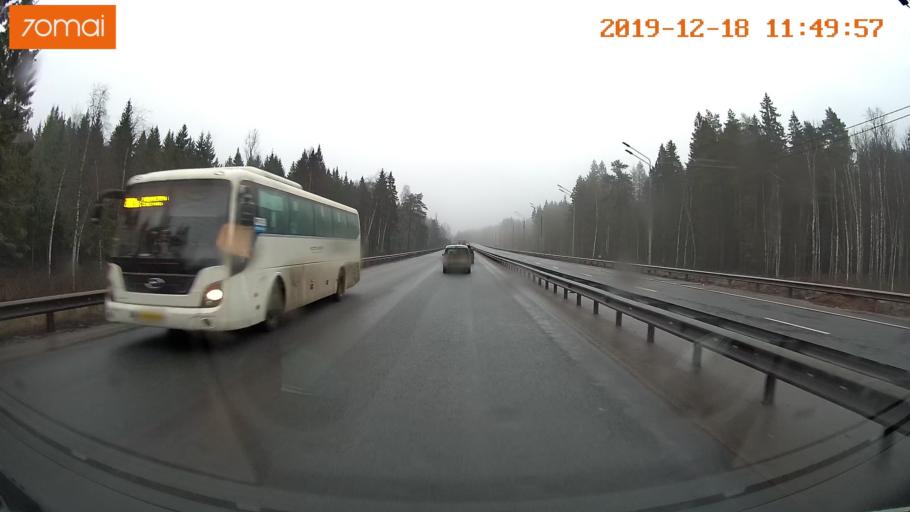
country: RU
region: Moskovskaya
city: Yershovo
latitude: 55.7819
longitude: 36.9153
